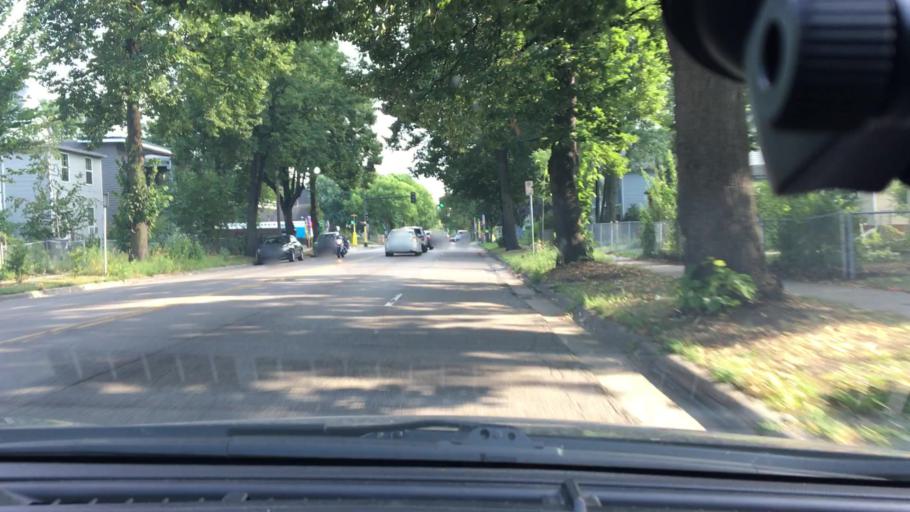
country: US
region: Minnesota
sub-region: Hennepin County
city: Minneapolis
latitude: 44.9424
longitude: -93.2475
